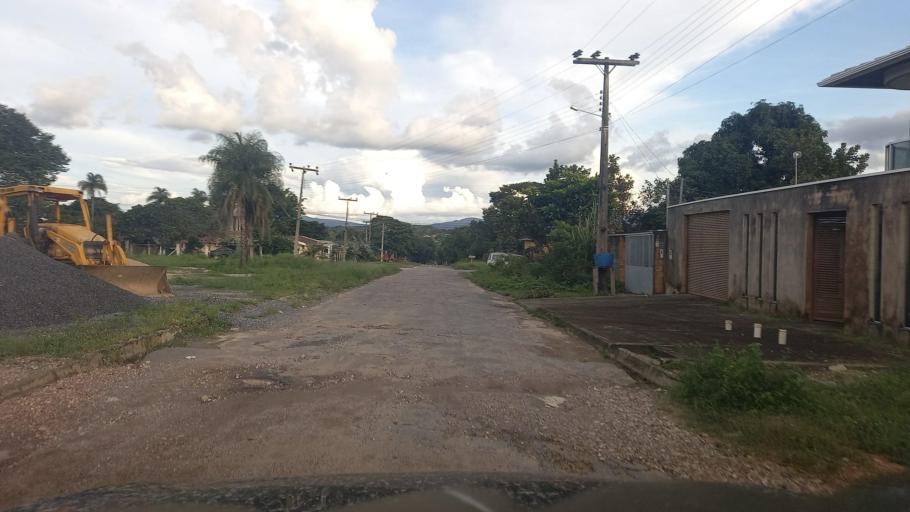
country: BR
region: Goias
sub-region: Cavalcante
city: Cavalcante
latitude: -13.7925
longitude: -47.4564
